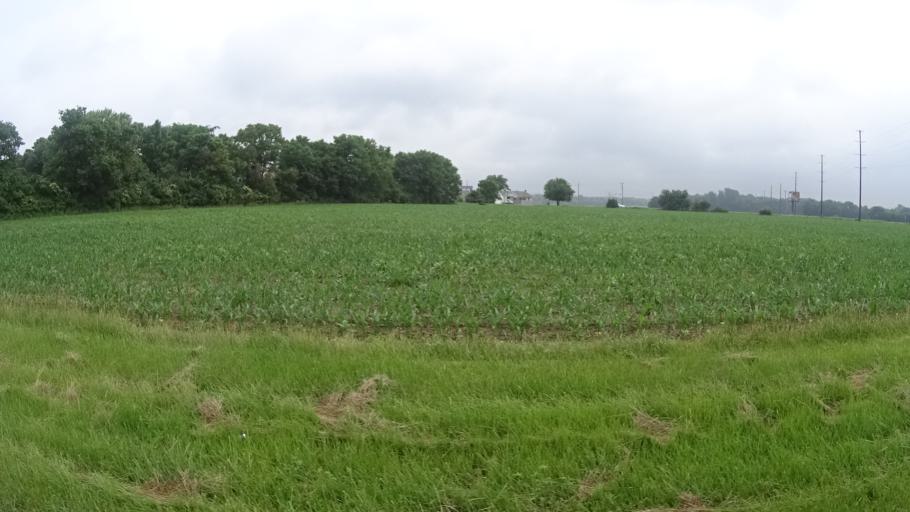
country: US
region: Ohio
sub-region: Erie County
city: Sandusky
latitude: 41.3544
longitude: -82.7550
